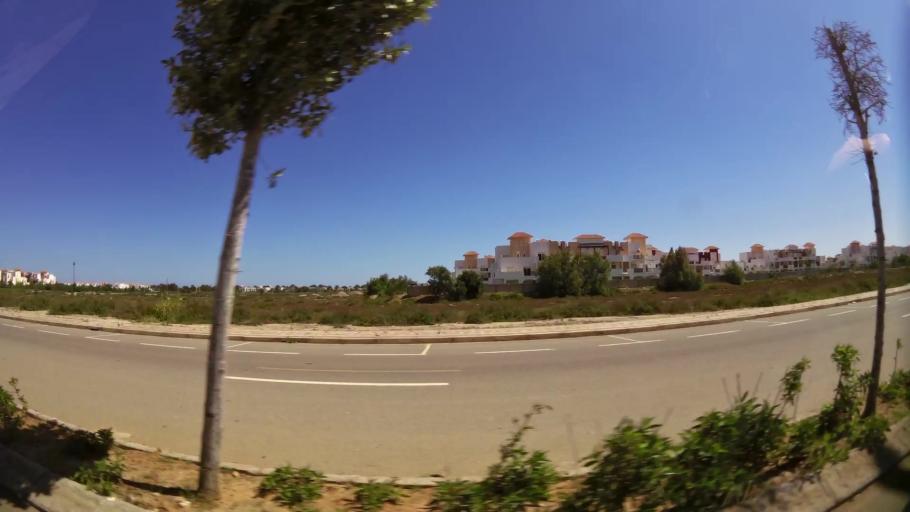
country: MA
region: Oriental
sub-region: Berkane-Taourirt
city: Madagh
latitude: 35.1012
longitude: -2.3103
